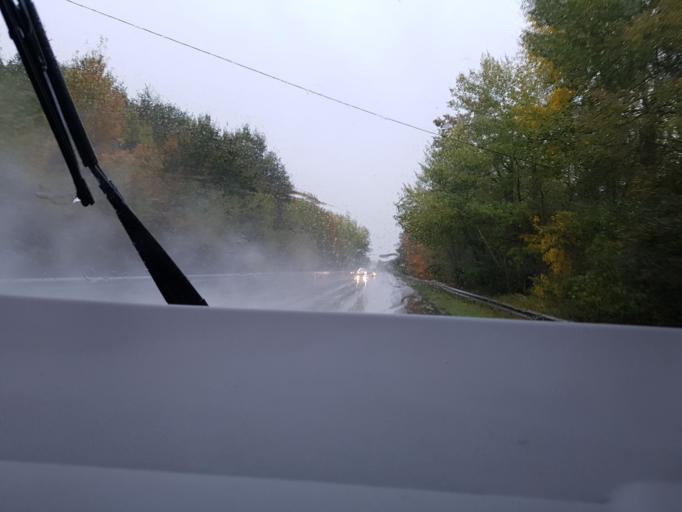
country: FR
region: Aquitaine
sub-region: Departement de la Gironde
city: Saint-Louis-de-Montferrand
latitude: 44.9603
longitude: -0.5053
